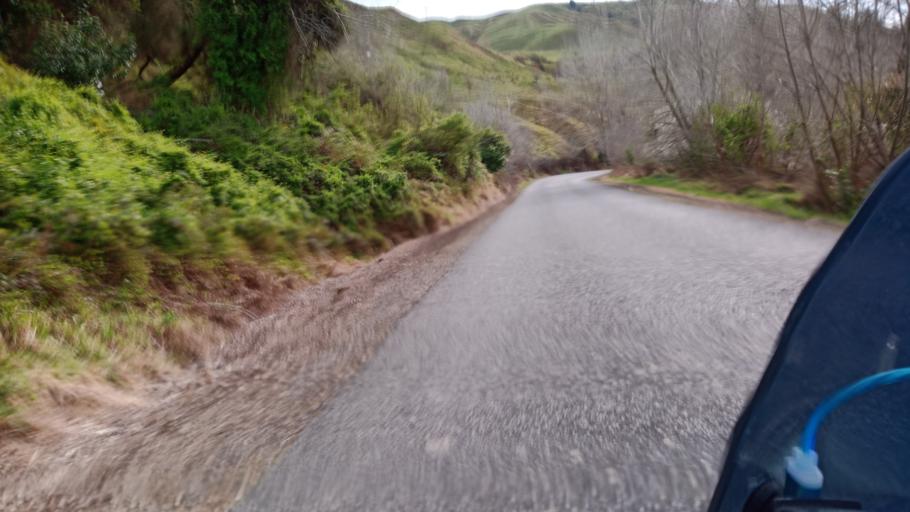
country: NZ
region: Hawke's Bay
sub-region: Wairoa District
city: Wairoa
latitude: -38.7913
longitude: 177.4332
